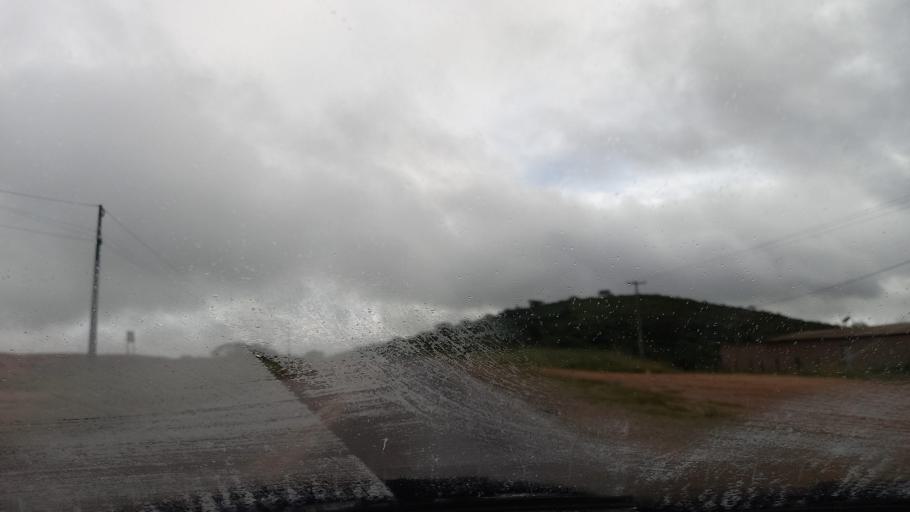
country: BR
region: Pernambuco
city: Garanhuns
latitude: -8.8589
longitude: -36.5116
